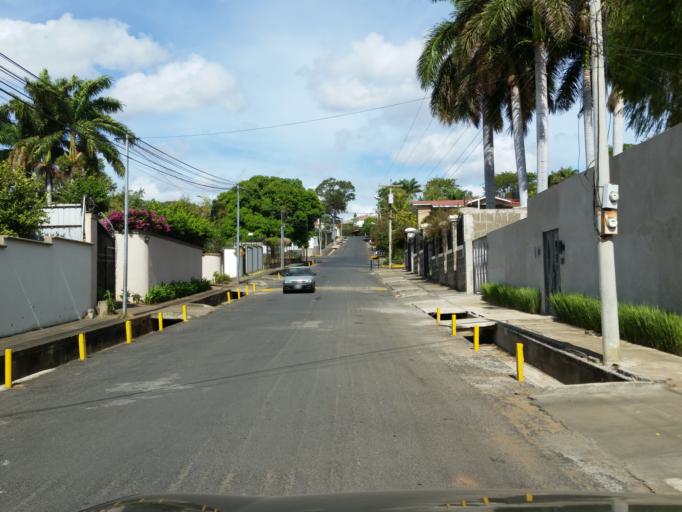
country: NI
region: Managua
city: Managua
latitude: 12.0800
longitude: -86.2385
